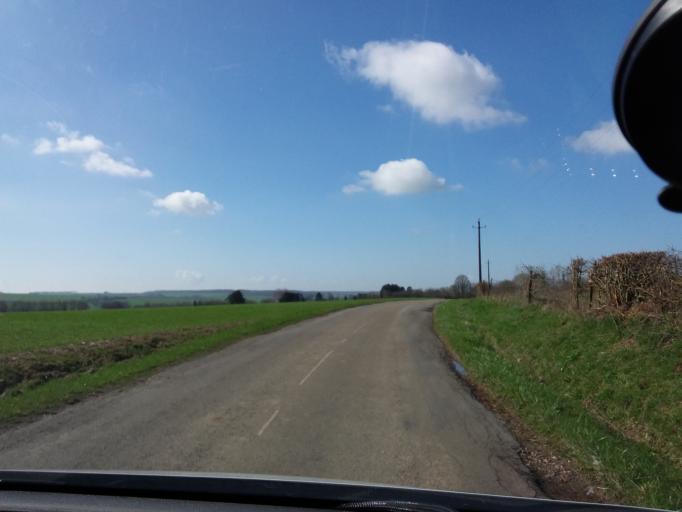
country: FR
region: Picardie
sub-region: Departement de l'Aisne
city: Origny-en-Thierache
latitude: 49.8155
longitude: 4.0291
